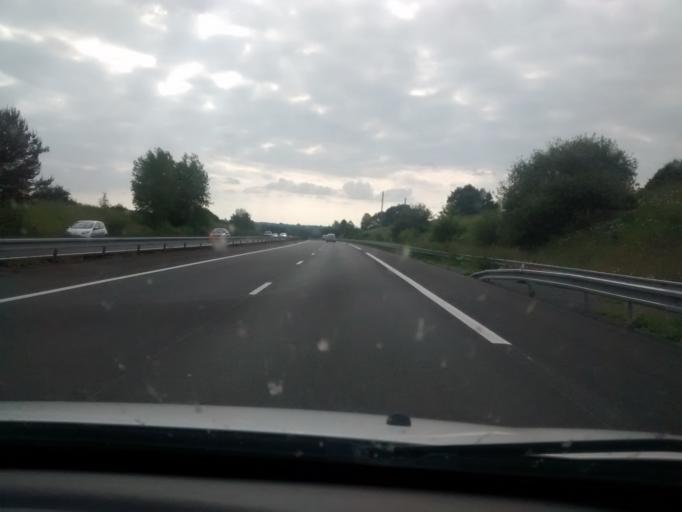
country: FR
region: Pays de la Loire
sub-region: Departement de la Mayenne
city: Vaiges
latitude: 48.0522
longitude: -0.4188
